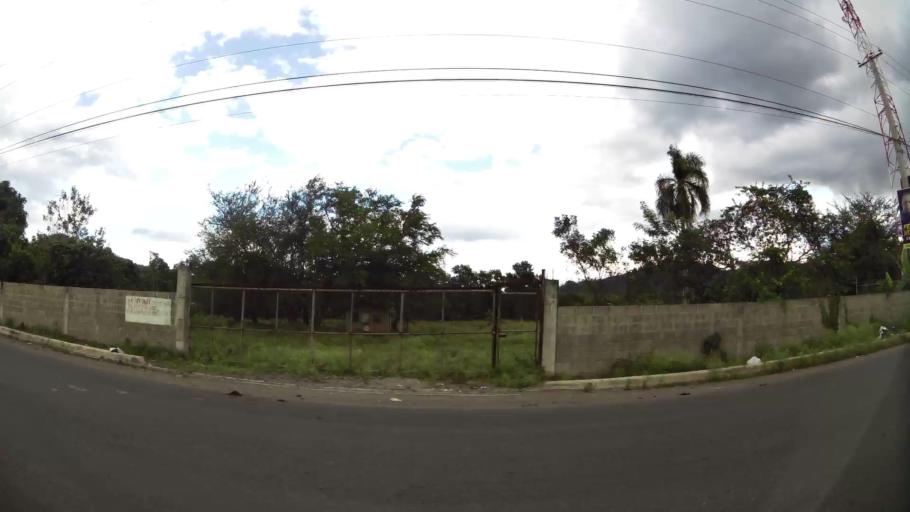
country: DO
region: Monsenor Nouel
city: Bonao
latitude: 18.9545
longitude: -70.4034
